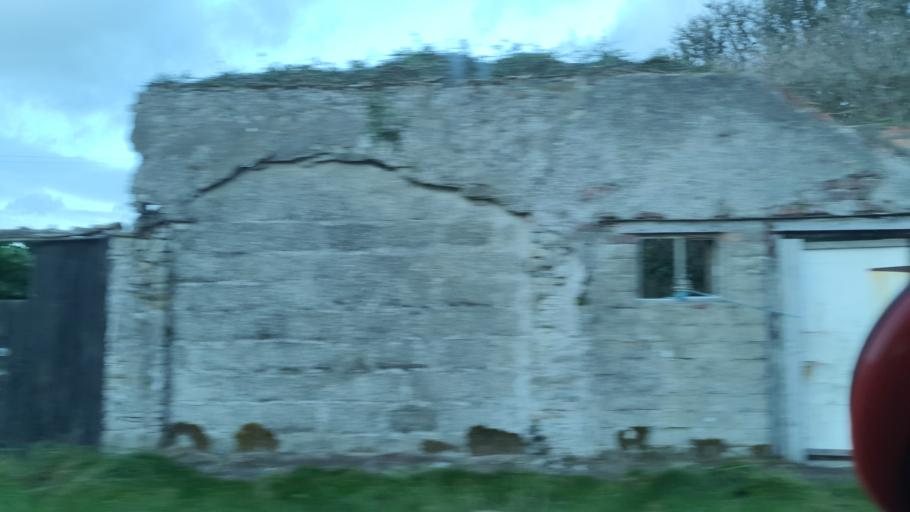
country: IE
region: Leinster
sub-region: Lu
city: Carlingford
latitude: 54.0402
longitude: -6.1030
